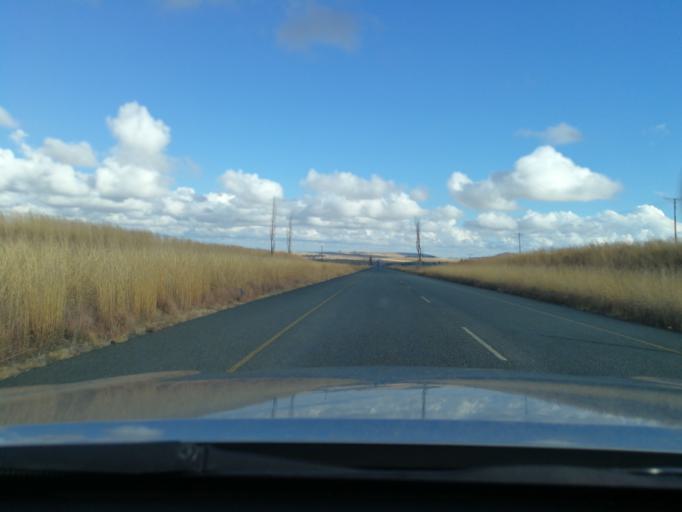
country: ZA
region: Orange Free State
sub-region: Thabo Mofutsanyana District Municipality
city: Reitz
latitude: -27.9285
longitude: 28.3878
